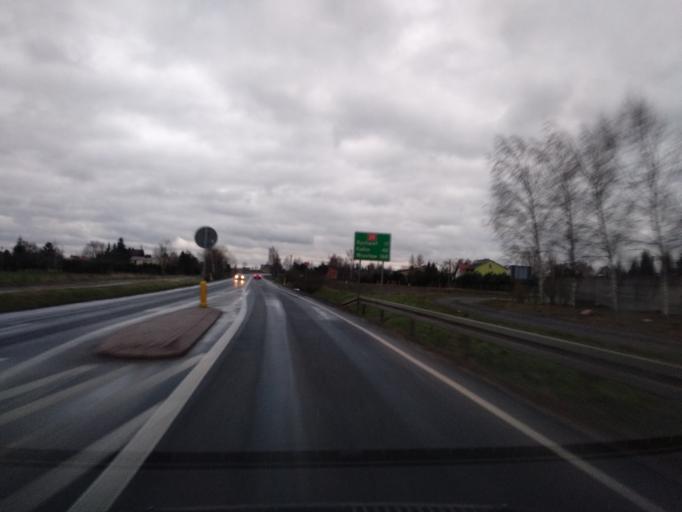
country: PL
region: Greater Poland Voivodeship
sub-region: Powiat koninski
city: Stare Miasto
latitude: 52.1576
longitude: 18.2054
